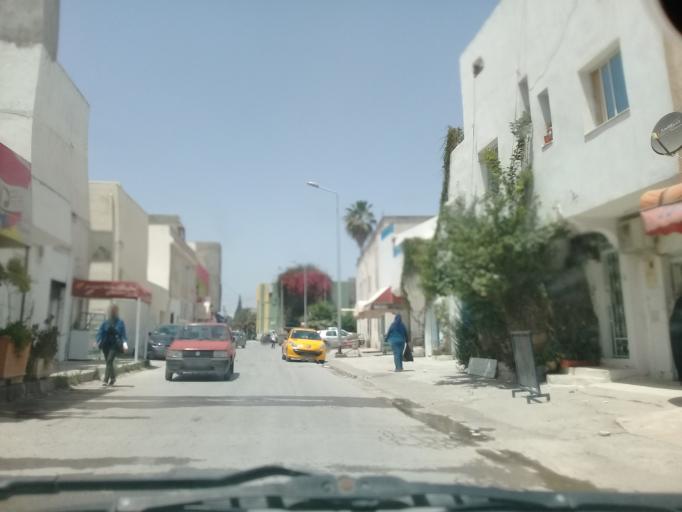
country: TN
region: Ariana
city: Ariana
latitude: 36.8318
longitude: 10.1968
